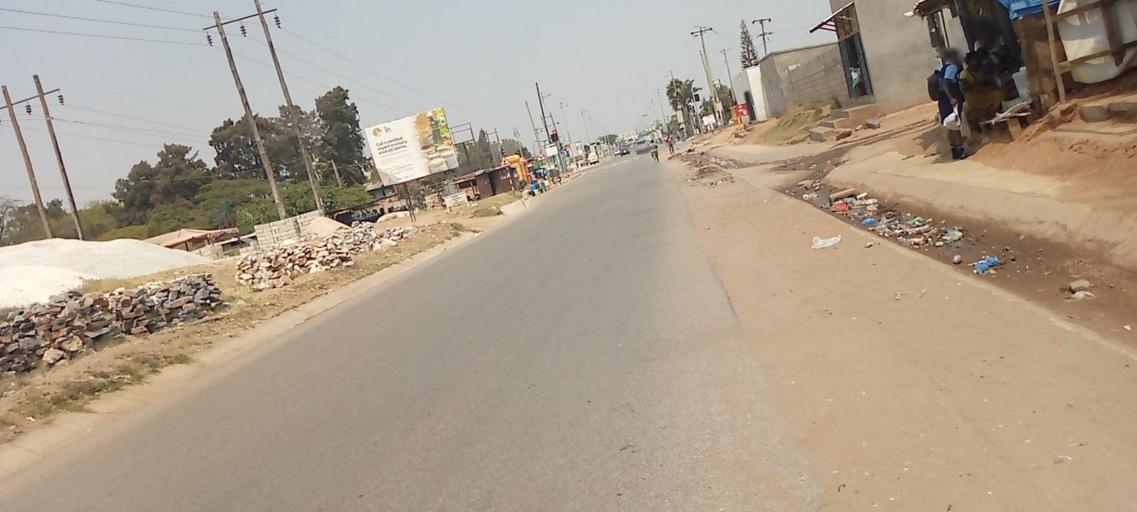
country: ZM
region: Lusaka
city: Lusaka
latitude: -15.4079
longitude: 28.3519
